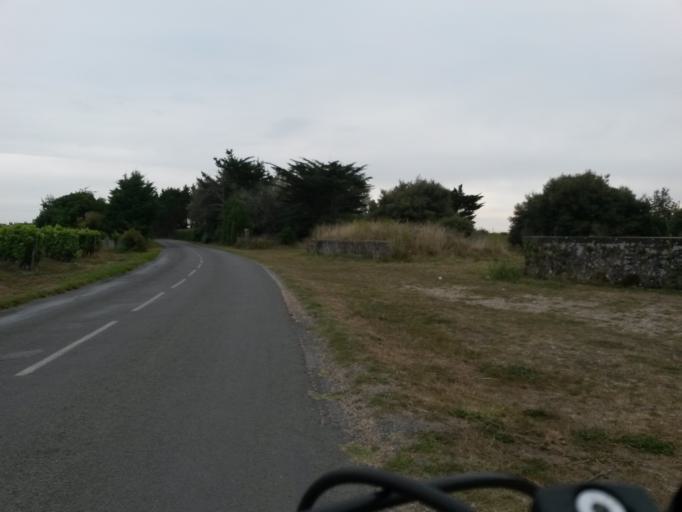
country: FR
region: Poitou-Charentes
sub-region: Departement de la Charente-Maritime
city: Dolus-d'Oleron
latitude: 45.9369
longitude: -1.3459
